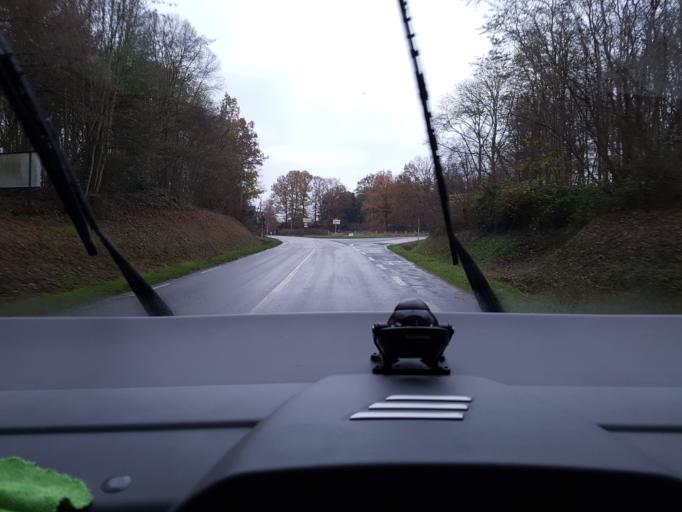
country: FR
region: Haute-Normandie
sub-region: Departement de l'Eure
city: Beaumont-le-Roger
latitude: 49.0846
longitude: 0.7893
